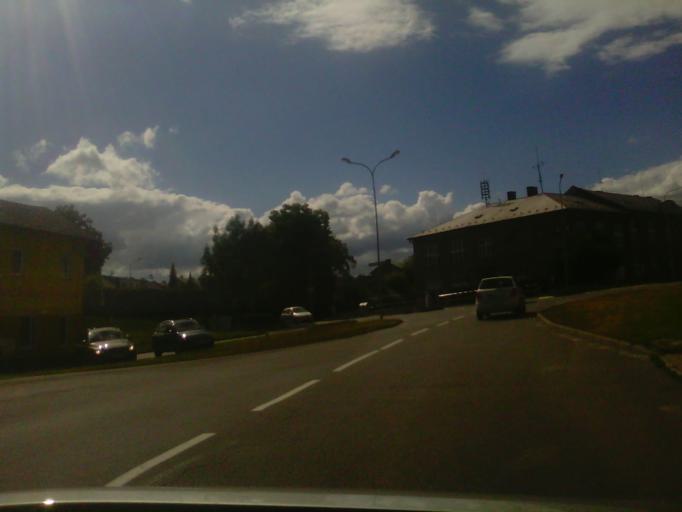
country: CZ
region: Olomoucky
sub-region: Okres Olomouc
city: Olomouc
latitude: 49.5688
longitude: 17.2361
